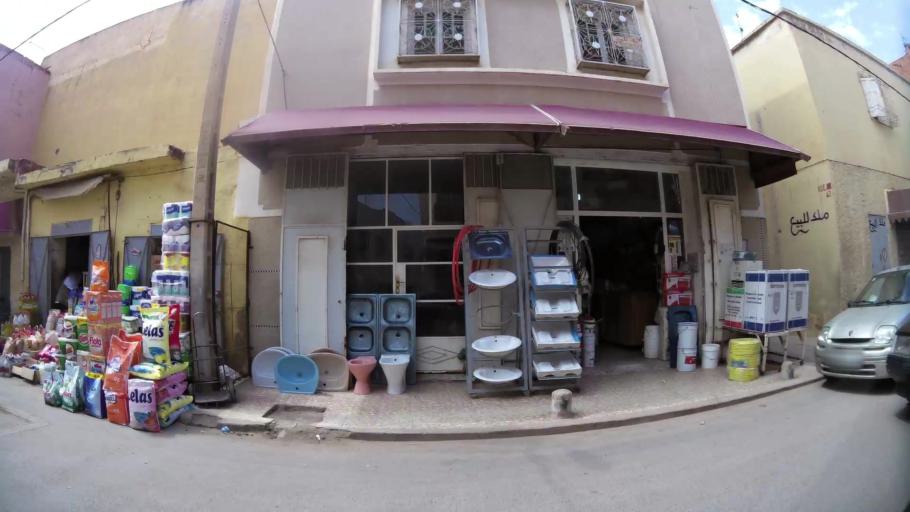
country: MA
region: Oriental
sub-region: Oujda-Angad
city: Oujda
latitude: 34.6810
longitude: -1.9031
